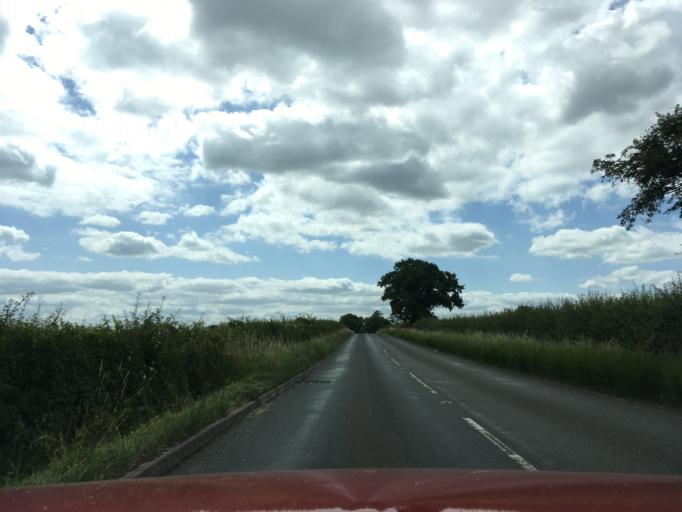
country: GB
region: England
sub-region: Milton Keynes
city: Shenley Church End
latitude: 51.9832
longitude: -0.8267
